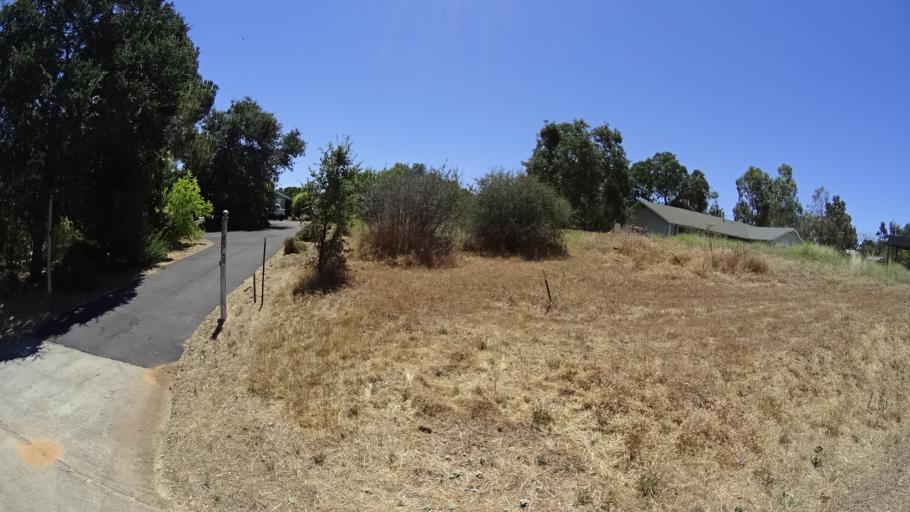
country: US
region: California
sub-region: Calaveras County
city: Rancho Calaveras
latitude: 38.1456
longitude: -120.8408
